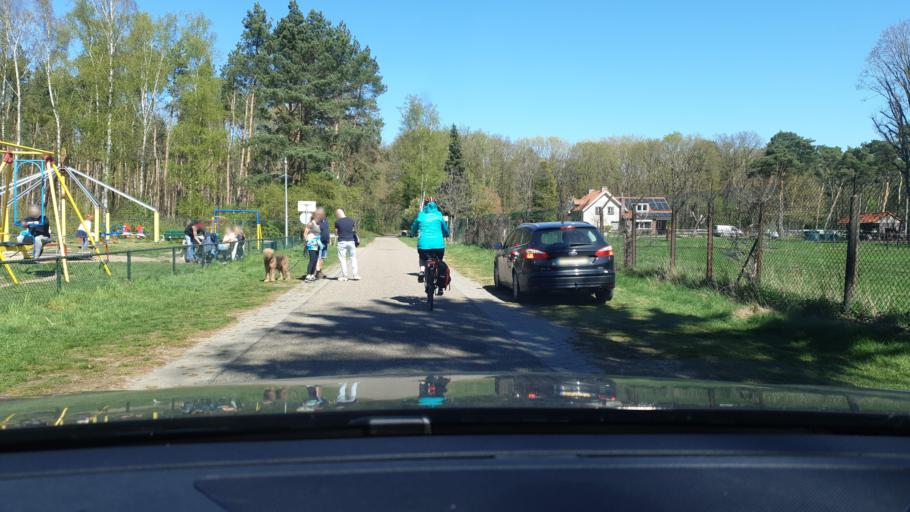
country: NL
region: Limburg
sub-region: Gemeente Venlo
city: Arcen
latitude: 51.4325
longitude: 6.1292
